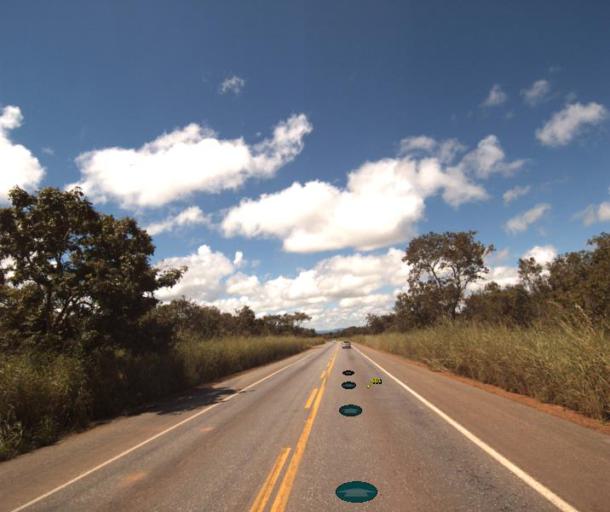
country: BR
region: Goias
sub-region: Jaragua
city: Jaragua
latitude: -15.8980
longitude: -49.2344
